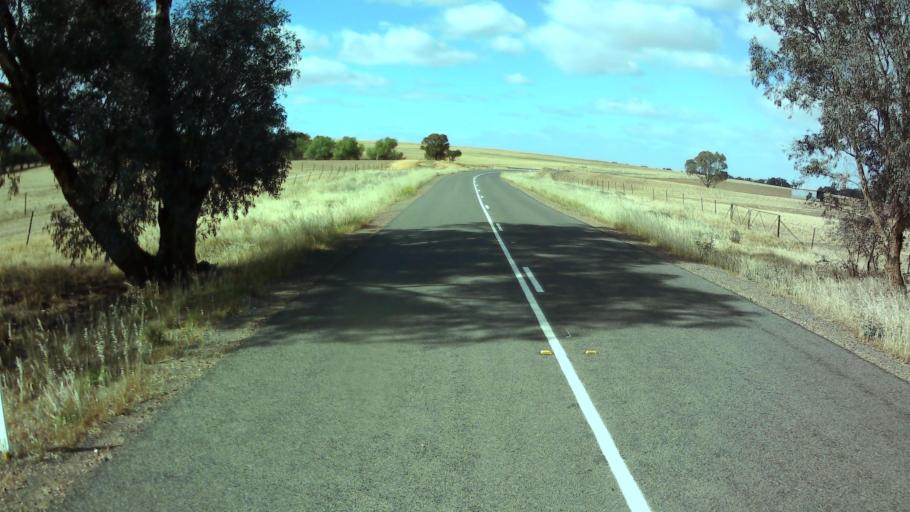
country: AU
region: New South Wales
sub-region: Weddin
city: Grenfell
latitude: -33.9740
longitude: 148.4255
